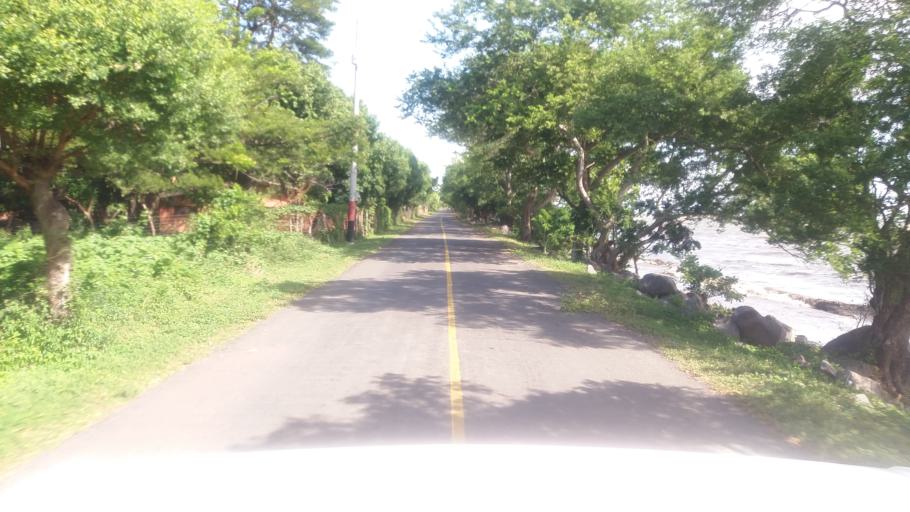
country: NI
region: Granada
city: Granada
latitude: 11.9775
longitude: -85.9417
